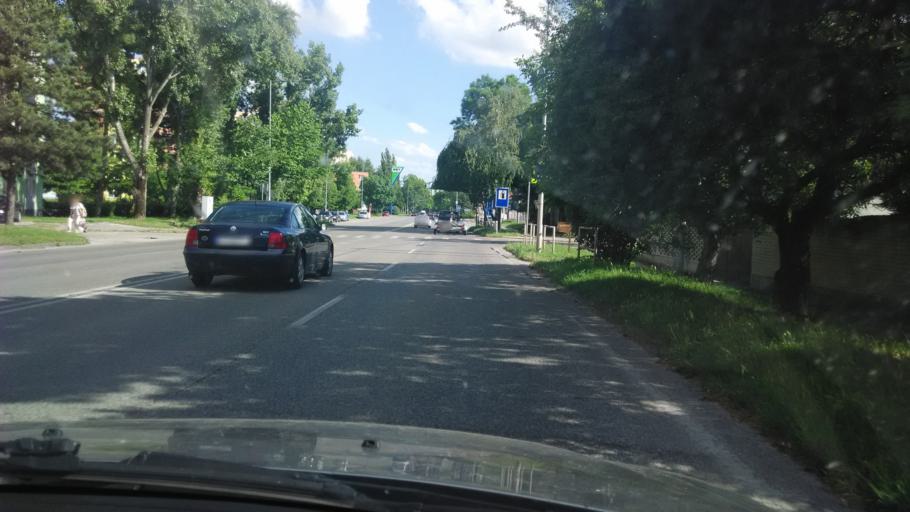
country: SK
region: Nitriansky
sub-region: Okres Nove Zamky
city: Nove Zamky
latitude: 47.9956
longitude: 18.1666
